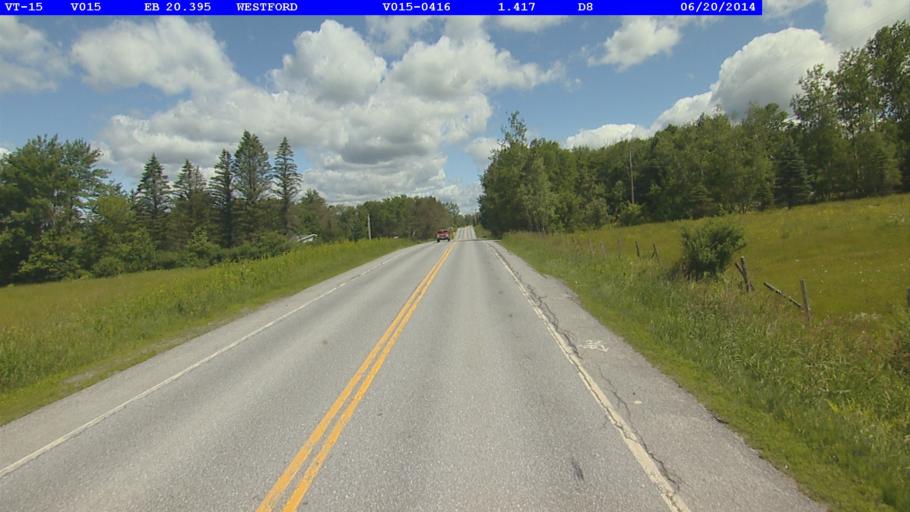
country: US
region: Vermont
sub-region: Chittenden County
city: Jericho
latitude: 44.6140
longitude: -72.9288
